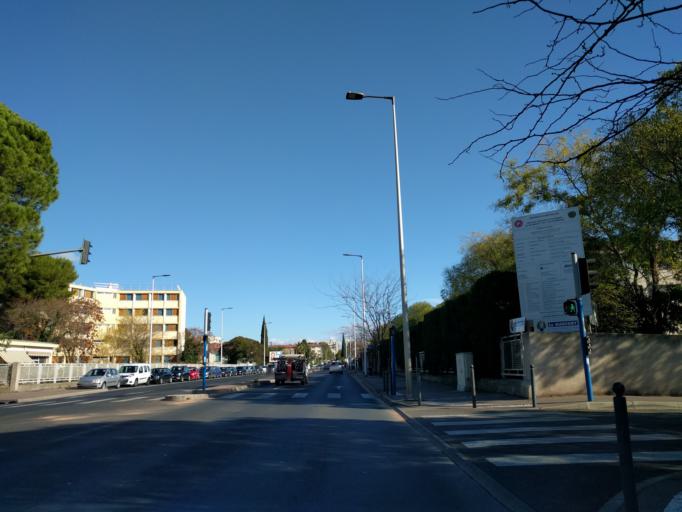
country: FR
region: Languedoc-Roussillon
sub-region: Departement de l'Herault
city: Montpellier
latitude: 43.6223
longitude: 3.8600
